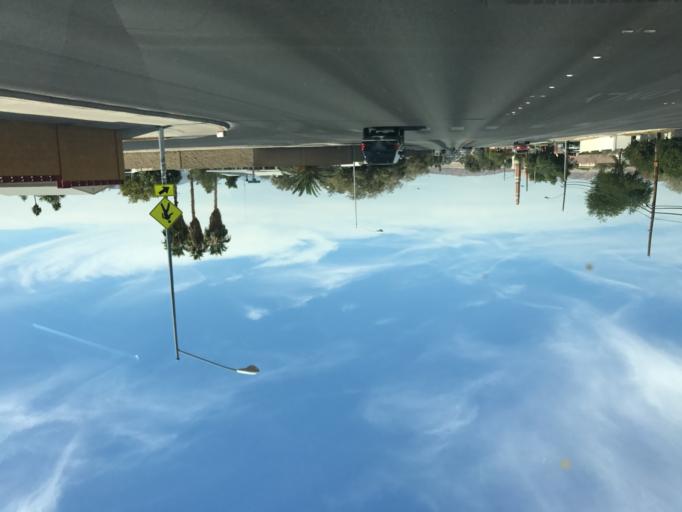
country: US
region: Nevada
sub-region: Clark County
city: Winchester
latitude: 36.1296
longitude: -115.0748
